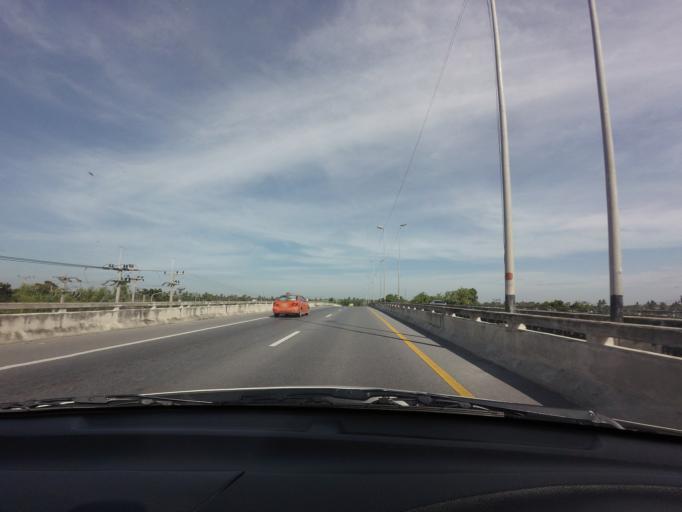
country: TH
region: Suphan Buri
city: Suphan Buri
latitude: 14.4543
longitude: 100.0844
